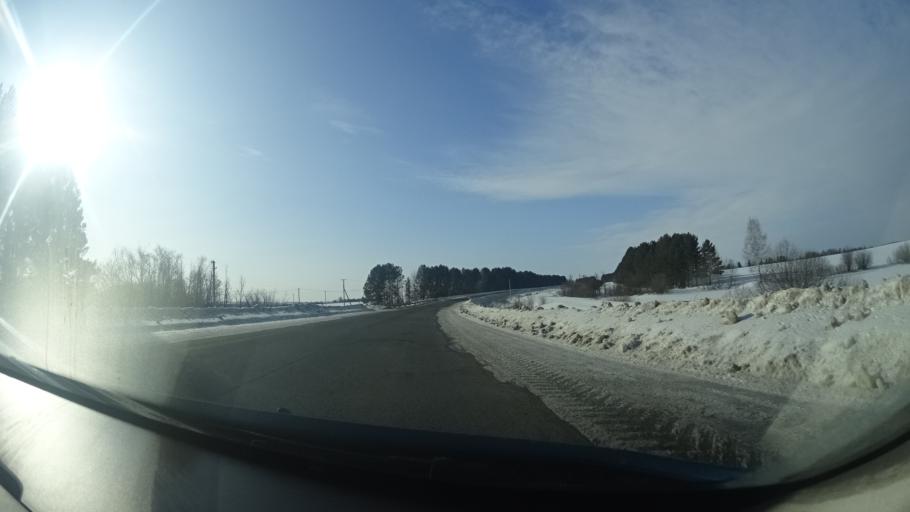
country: RU
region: Perm
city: Kuyeda
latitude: 56.4868
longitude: 55.5983
